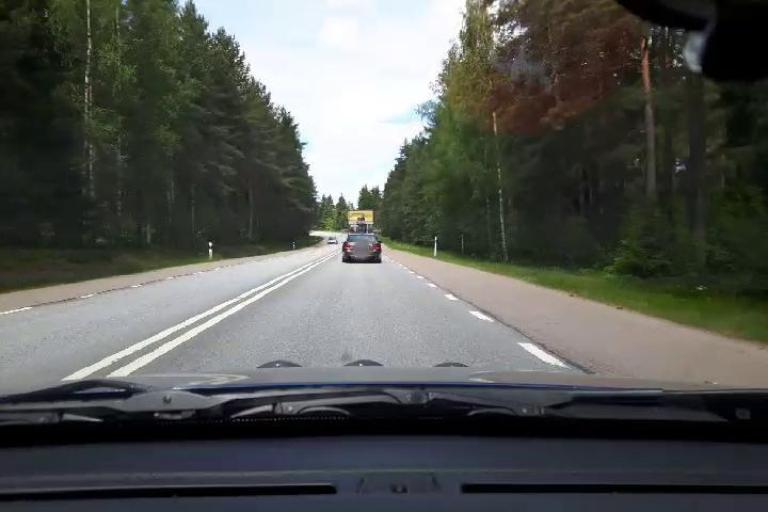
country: SE
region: Uppsala
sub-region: Osthammars Kommun
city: Bjorklinge
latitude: 60.0450
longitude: 17.5507
